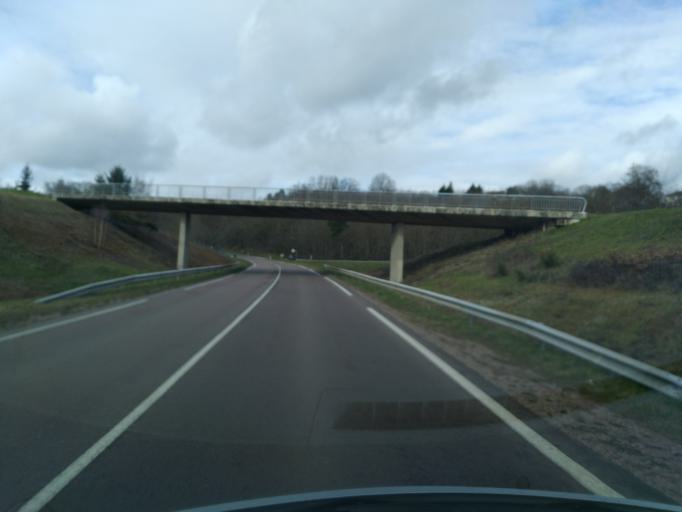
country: FR
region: Bourgogne
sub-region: Departement de Saone-et-Loire
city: Montcenis
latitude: 46.7894
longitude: 4.4030
